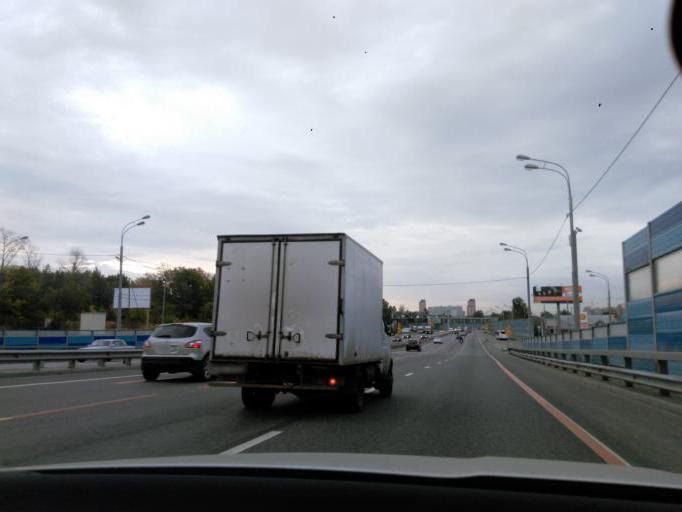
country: RU
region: Moscow
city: Severnyy
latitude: 55.9473
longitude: 37.5406
